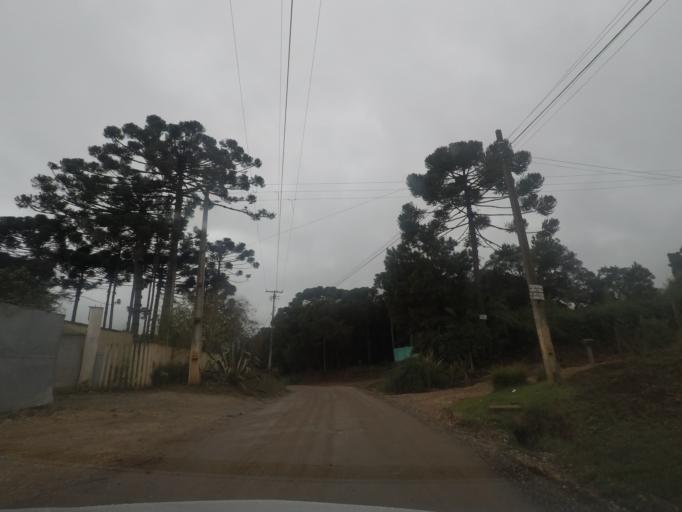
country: BR
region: Parana
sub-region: Campina Grande Do Sul
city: Campina Grande do Sul
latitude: -25.3053
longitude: -49.1155
